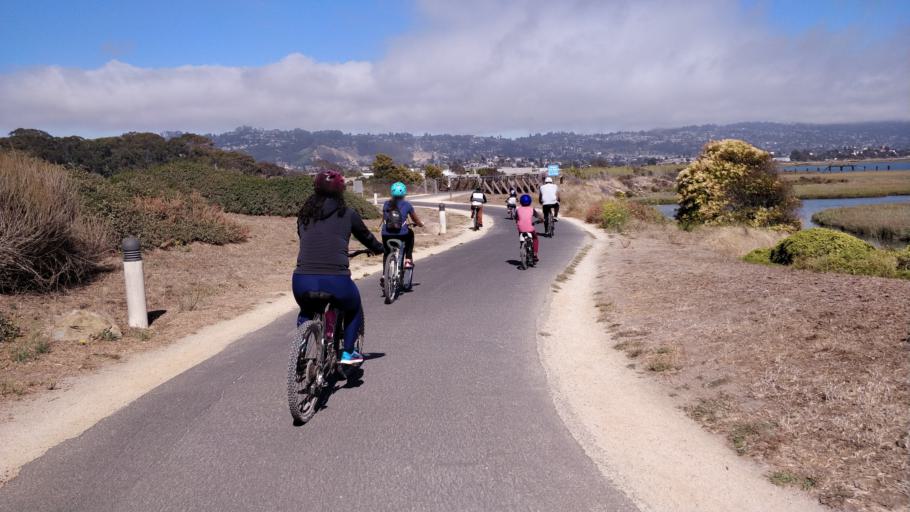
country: US
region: California
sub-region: Contra Costa County
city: El Cerrito
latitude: 37.9108
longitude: -122.3379
